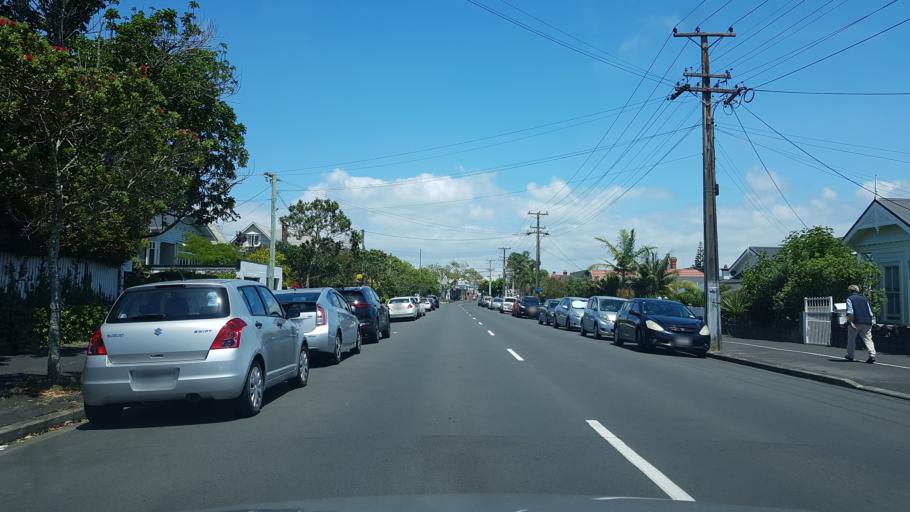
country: NZ
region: Auckland
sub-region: Auckland
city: Auckland
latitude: -36.8287
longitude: 174.7950
